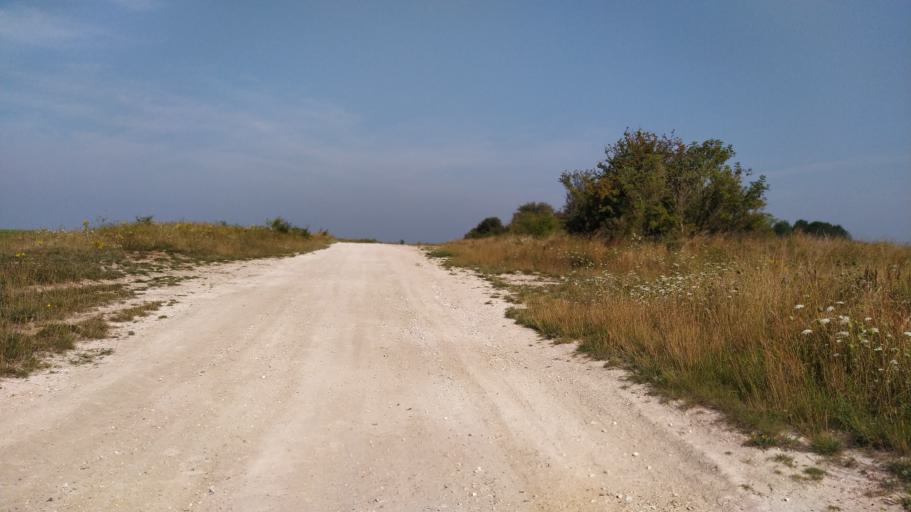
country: GB
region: England
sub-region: Wiltshire
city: Shrewton
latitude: 51.1846
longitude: -1.9509
